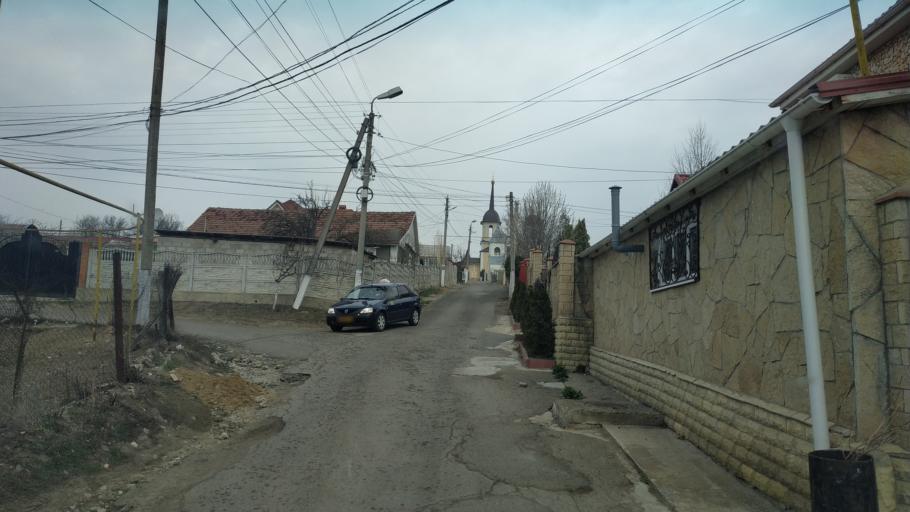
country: MD
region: Chisinau
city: Singera
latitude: 46.9351
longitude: 28.9920
